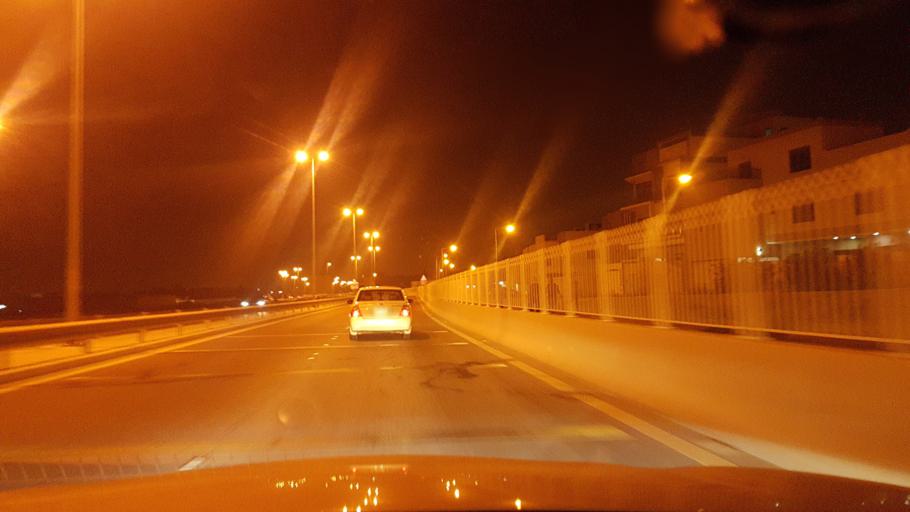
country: BH
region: Central Governorate
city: Dar Kulayb
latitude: 26.0842
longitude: 50.5021
